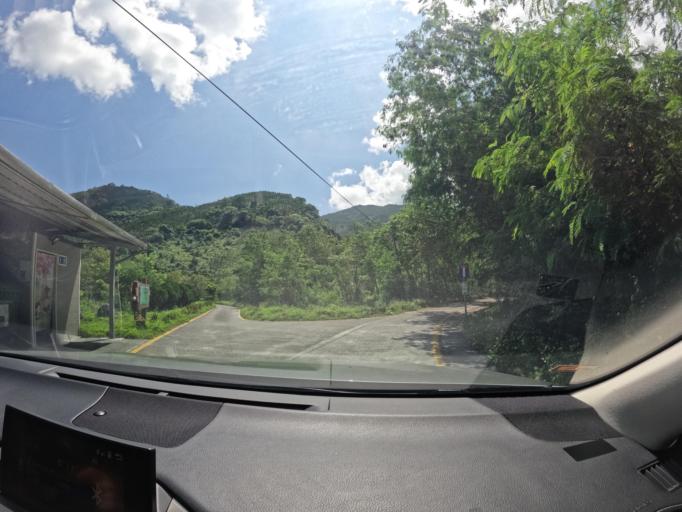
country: TW
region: Taiwan
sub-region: Hualien
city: Hualian
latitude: 23.6815
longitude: 121.3969
